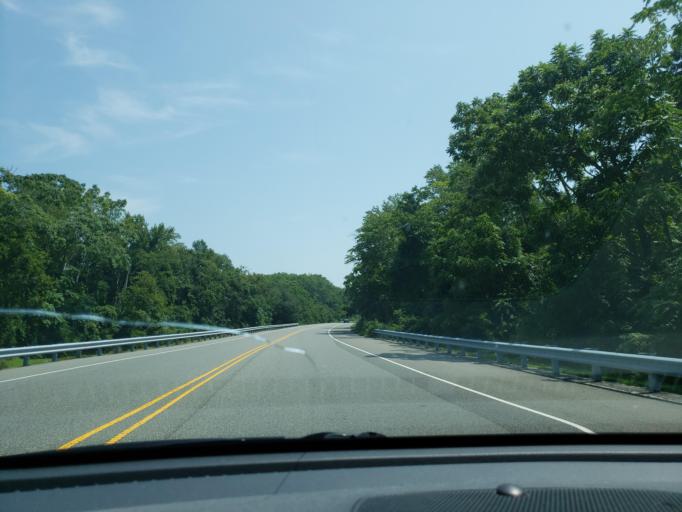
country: US
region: New Jersey
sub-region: Cape May County
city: North Cape May
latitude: 38.9737
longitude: -74.9343
